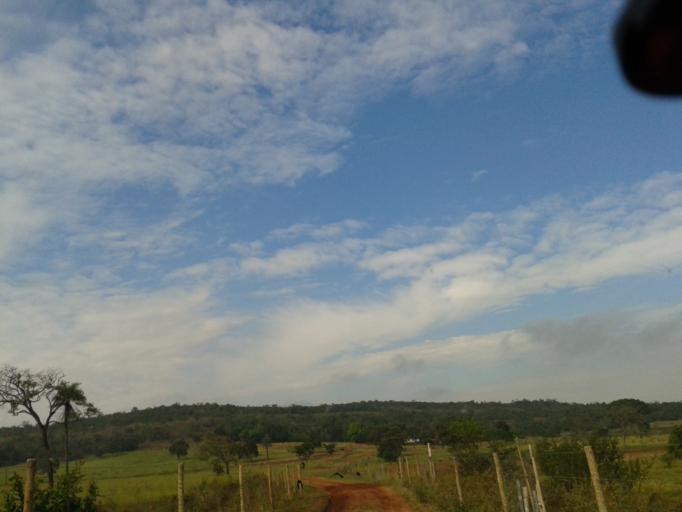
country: BR
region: Minas Gerais
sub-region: Campina Verde
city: Campina Verde
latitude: -19.3926
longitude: -49.6263
